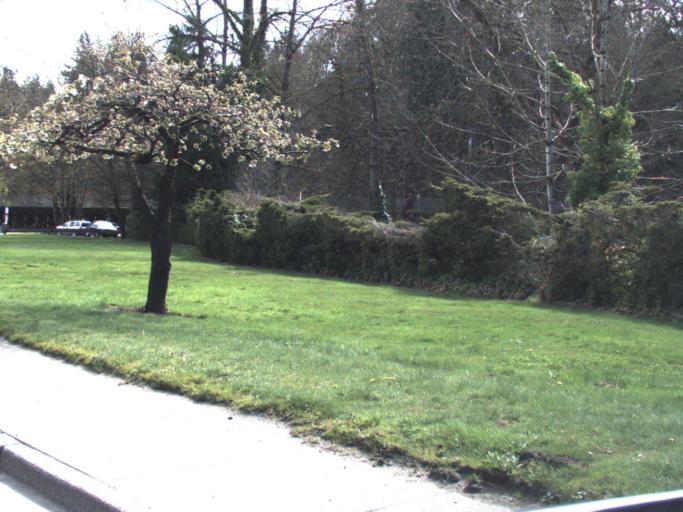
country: US
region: Washington
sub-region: King County
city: Fairwood
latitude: 47.4761
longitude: -122.1772
